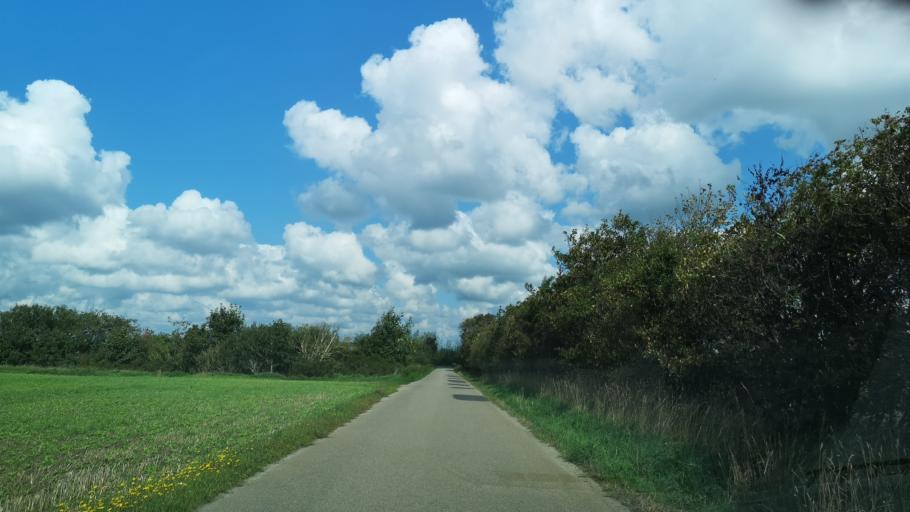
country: DK
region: Central Jutland
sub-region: Ringkobing-Skjern Kommune
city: Skjern
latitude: 55.9362
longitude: 8.4608
